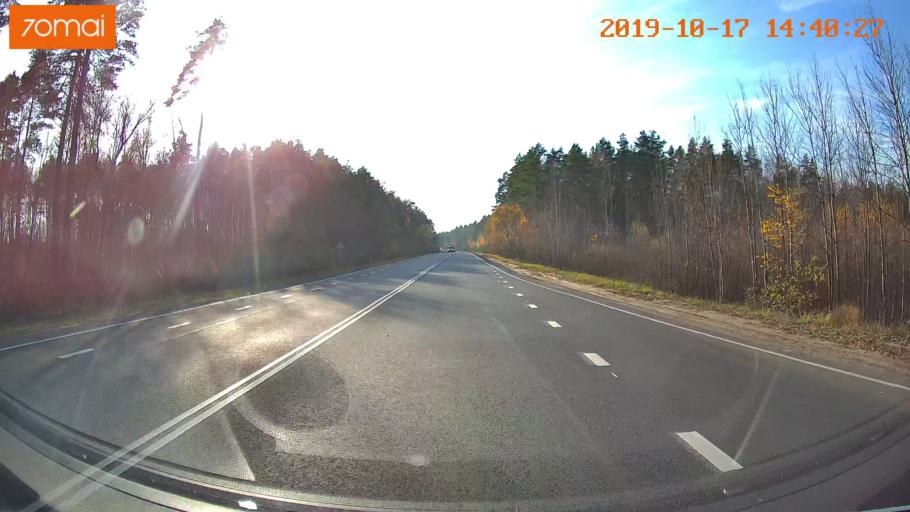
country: RU
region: Rjazan
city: Solotcha
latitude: 54.8549
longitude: 39.9569
